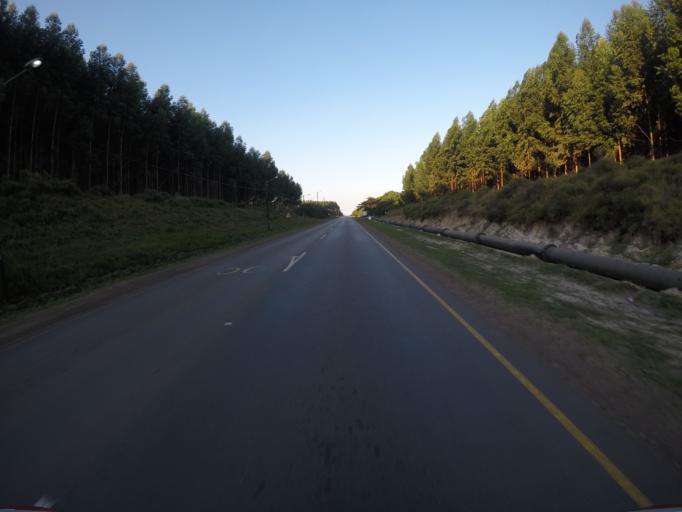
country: ZA
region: KwaZulu-Natal
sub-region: uThungulu District Municipality
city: KwaMbonambi
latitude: -28.6833
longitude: 32.1518
